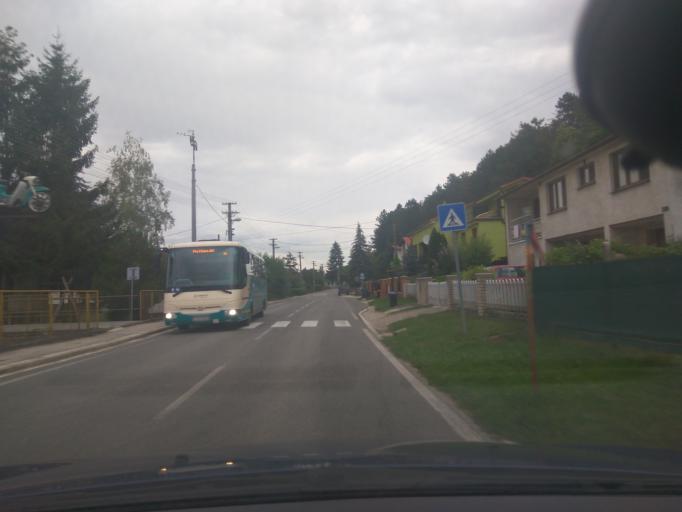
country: SK
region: Trnavsky
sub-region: Okres Trnava
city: Piestany
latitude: 48.6287
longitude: 17.8679
